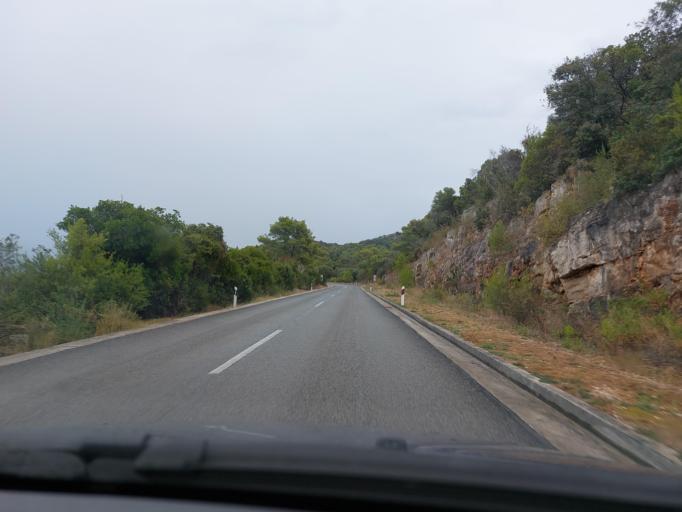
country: HR
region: Dubrovacko-Neretvanska
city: Smokvica
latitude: 42.7681
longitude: 16.8688
